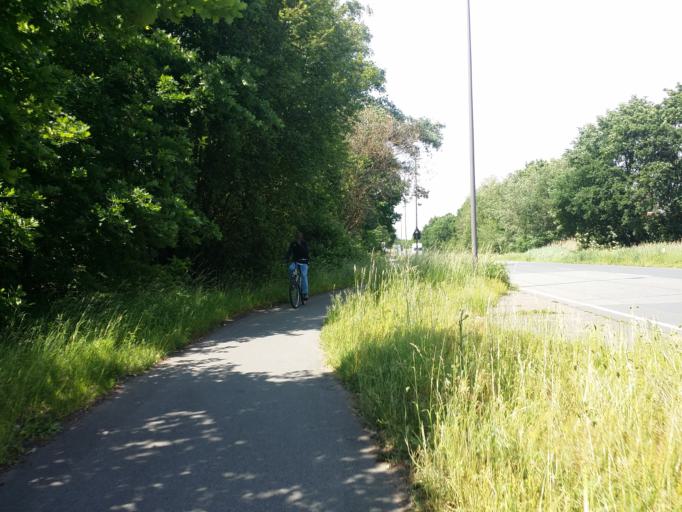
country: DE
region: Lower Saxony
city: Stuhr
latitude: 53.0855
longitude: 8.7480
